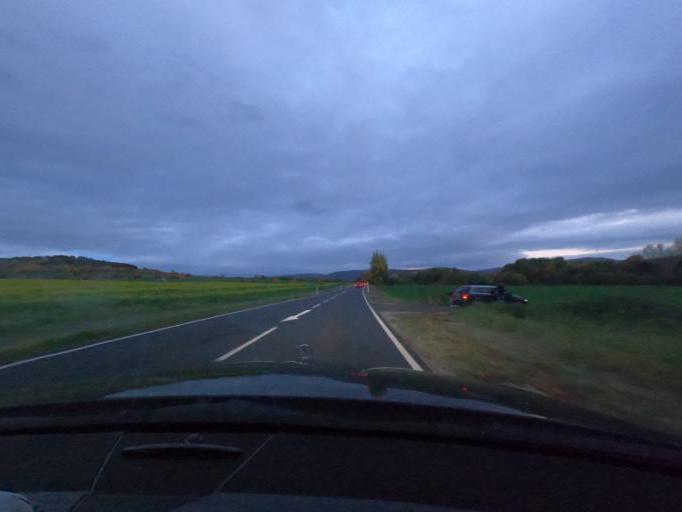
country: DE
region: Thuringia
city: Arenshausen
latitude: 51.3950
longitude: 9.9459
